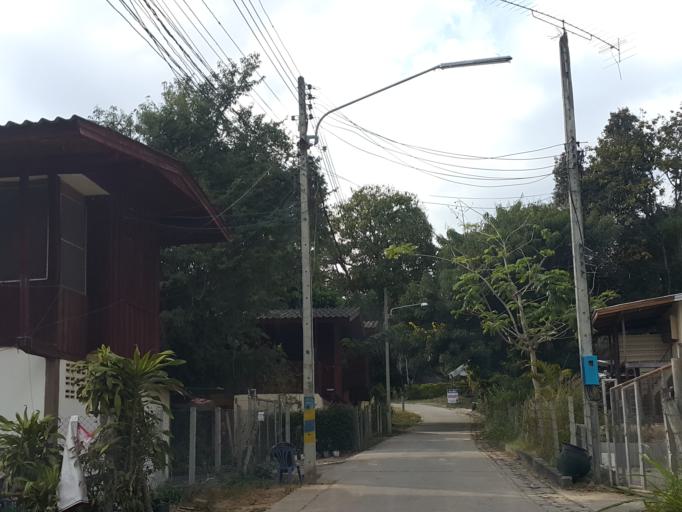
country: TH
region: Chiang Mai
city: Om Koi
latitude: 17.7992
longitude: 98.3569
